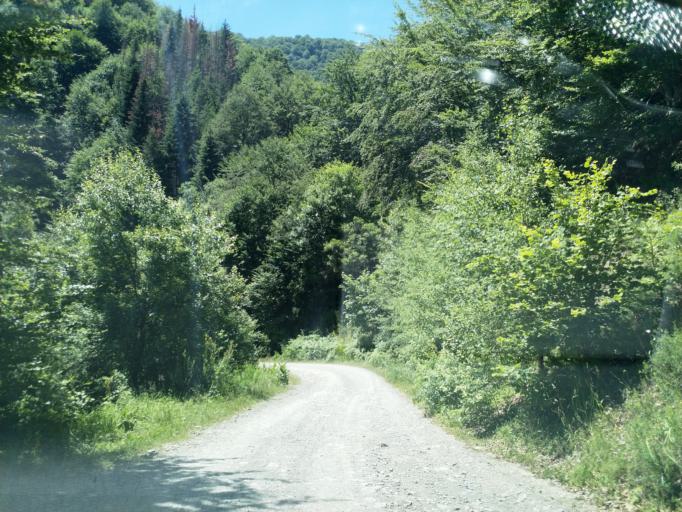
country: XK
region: Mitrovica
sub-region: Komuna e Leposaviqit
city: Leposaviq
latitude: 43.2788
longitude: 20.8673
